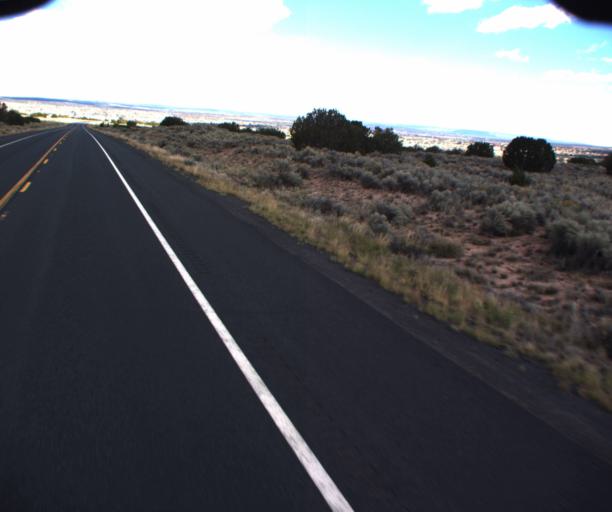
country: US
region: Arizona
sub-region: Apache County
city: Houck
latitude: 35.1756
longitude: -109.3380
